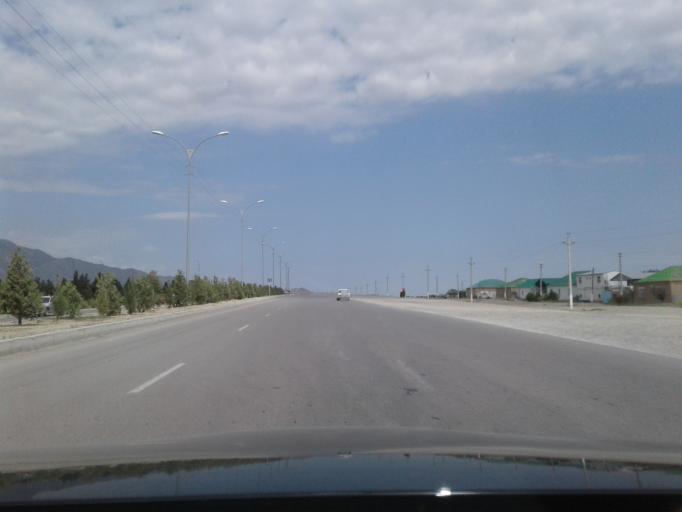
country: TM
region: Ahal
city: Baharly
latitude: 38.5239
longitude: 57.1788
